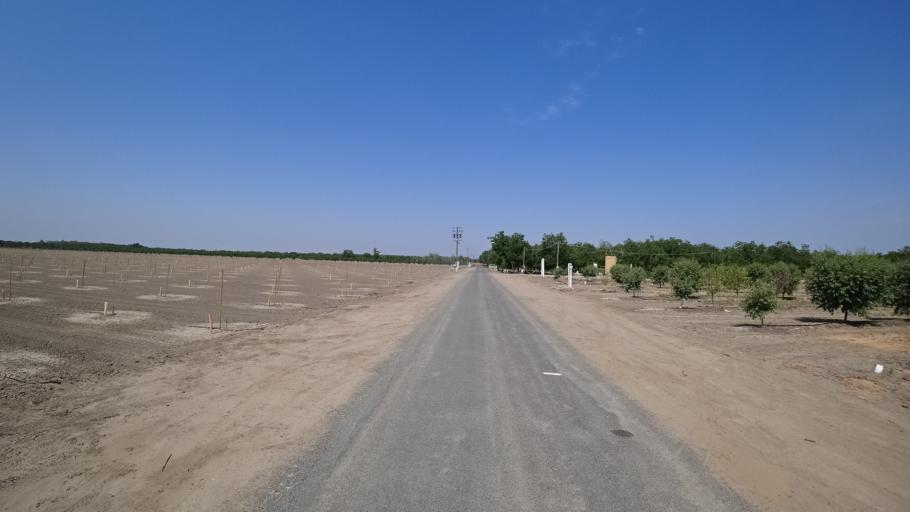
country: US
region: California
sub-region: Fresno County
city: Riverdale
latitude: 36.3948
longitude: -119.8042
